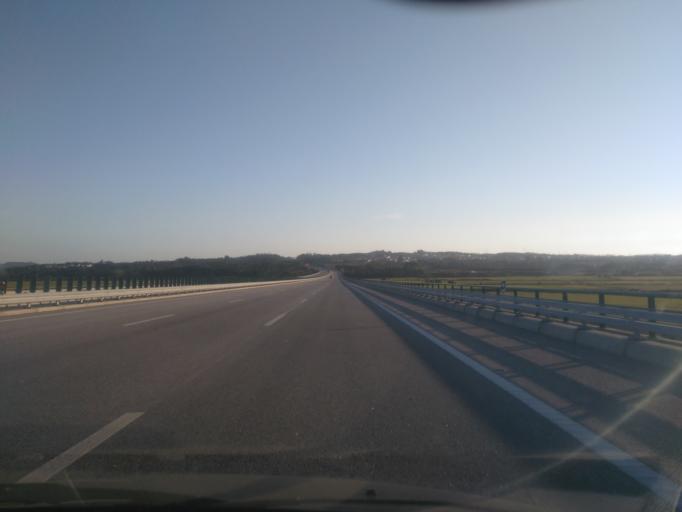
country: PT
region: Coimbra
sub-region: Figueira da Foz
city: Lavos
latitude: 40.0991
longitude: -8.7518
